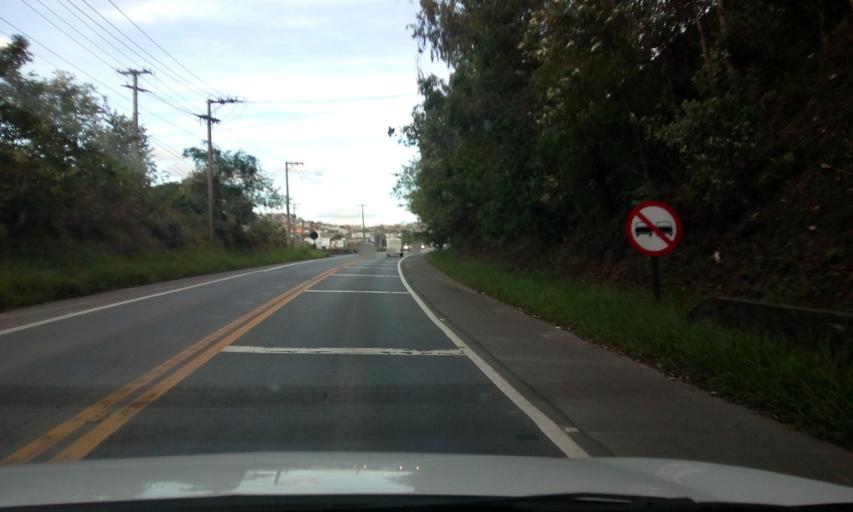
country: BR
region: Sao Paulo
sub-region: Itatiba
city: Itatiba
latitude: -23.0142
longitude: -46.8351
